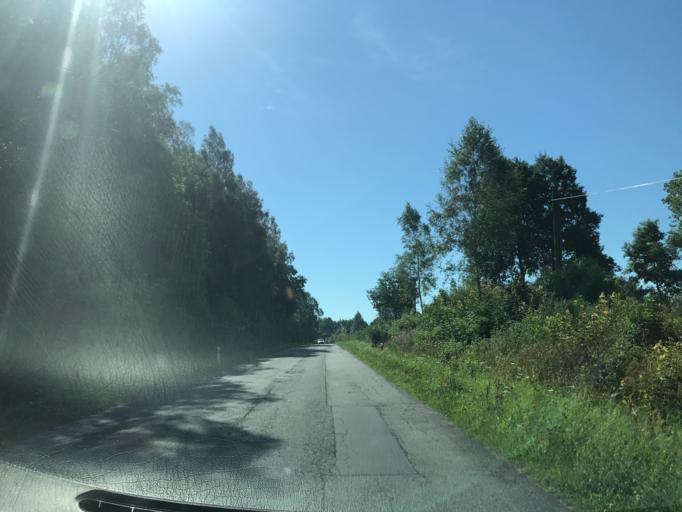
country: PL
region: Pomeranian Voivodeship
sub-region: Powiat bytowski
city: Czarna Dabrowka
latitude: 54.3487
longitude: 17.5822
